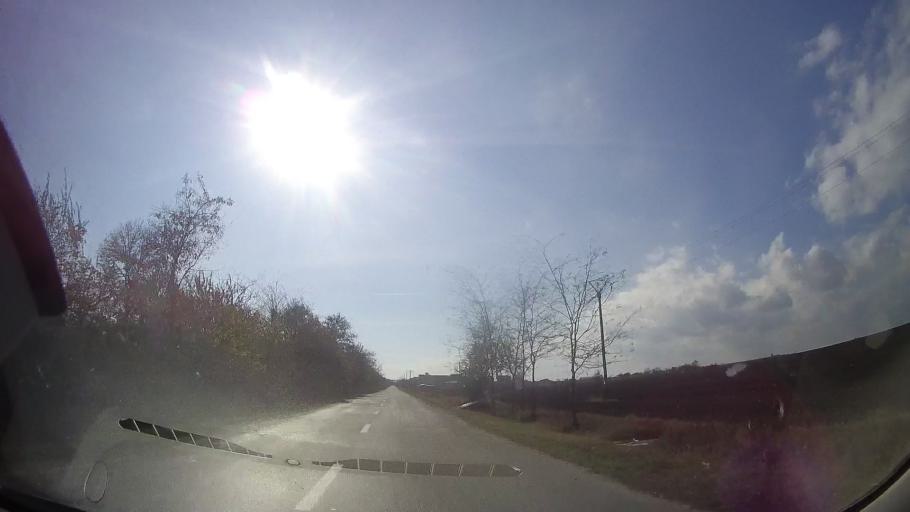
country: RO
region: Constanta
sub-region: Comuna Costinesti
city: Costinesti
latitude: 43.9605
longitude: 28.6360
